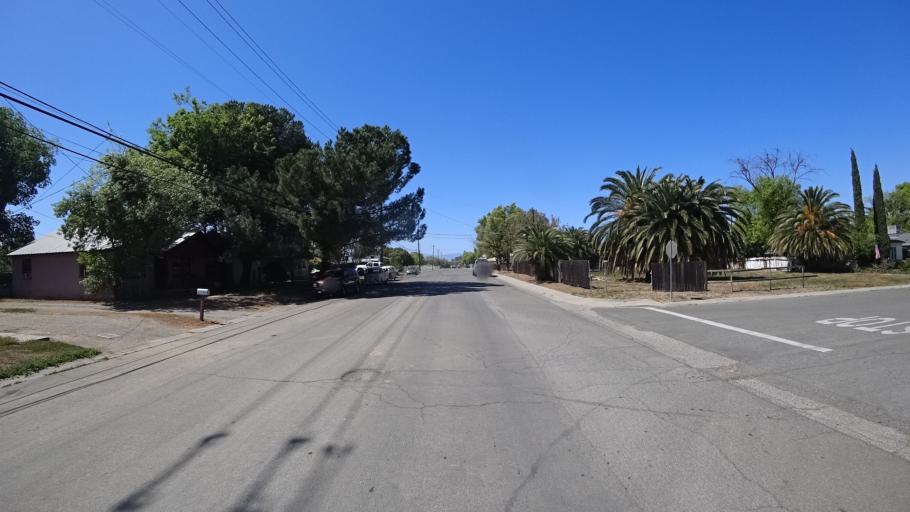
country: US
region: California
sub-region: Glenn County
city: Willows
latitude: 39.5268
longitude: -122.1996
